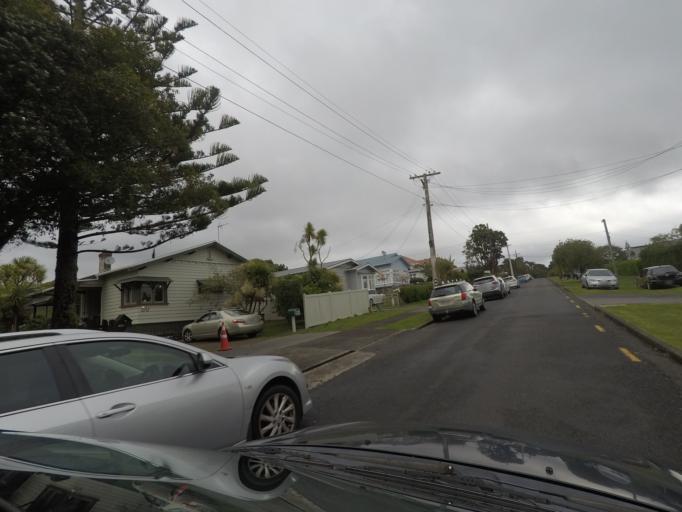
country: NZ
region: Auckland
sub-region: Auckland
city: Auckland
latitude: -36.8919
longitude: 174.7307
